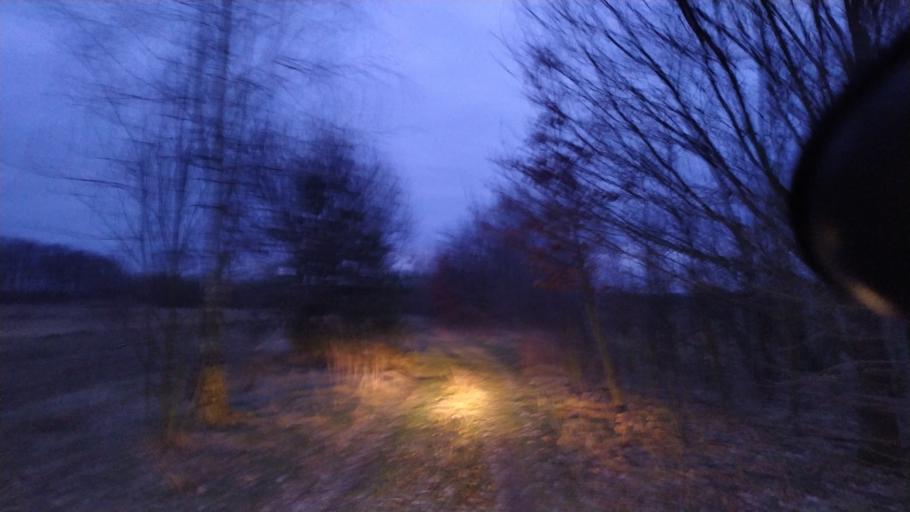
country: PL
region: Lublin Voivodeship
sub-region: Powiat lubartowski
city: Kamionka
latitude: 51.3912
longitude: 22.4316
